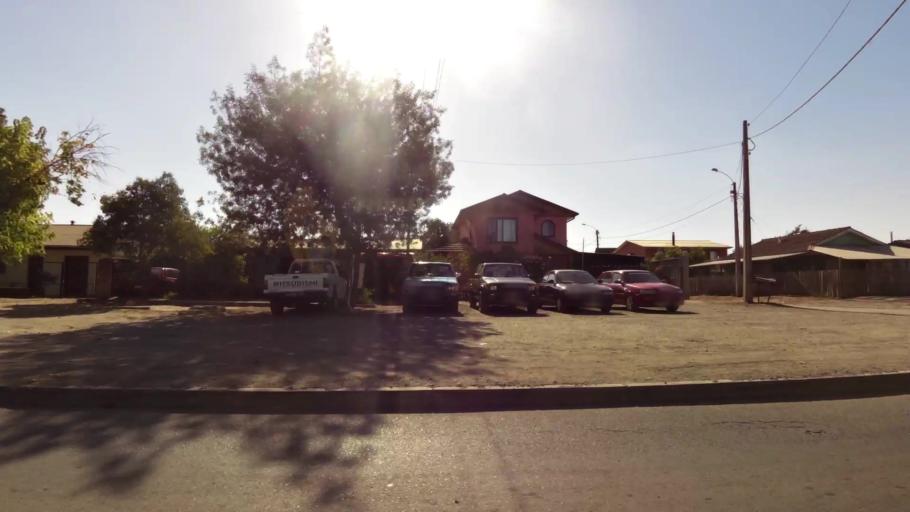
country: CL
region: Maule
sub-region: Provincia de Talca
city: Talca
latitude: -35.4470
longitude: -71.6489
